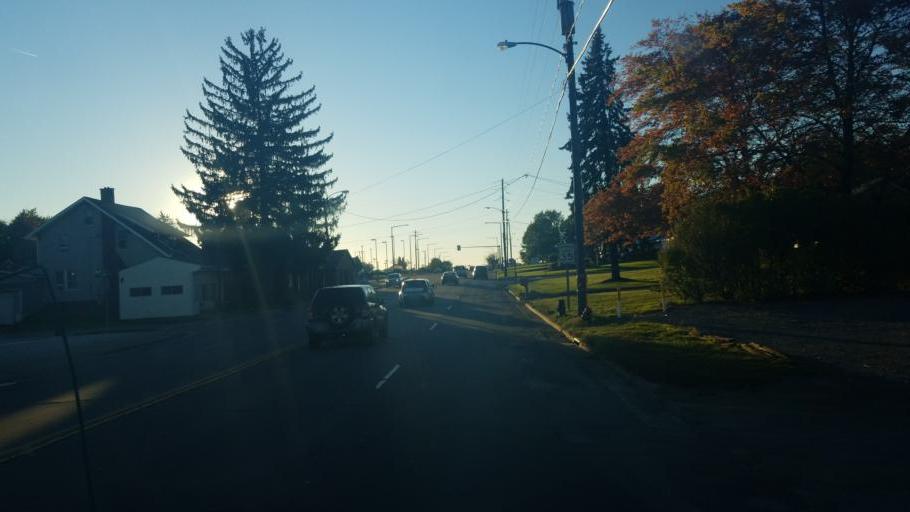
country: US
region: Ohio
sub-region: Stark County
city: Alliance
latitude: 40.9019
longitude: -81.1268
